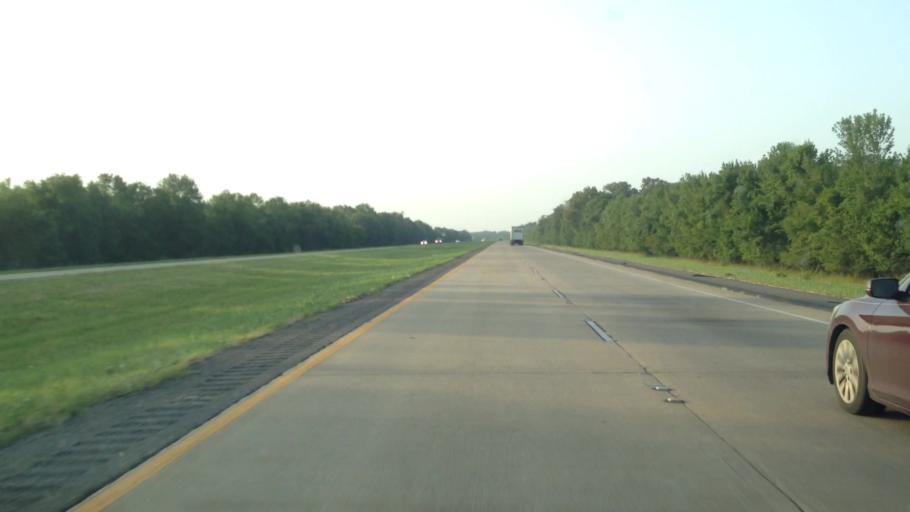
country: US
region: Louisiana
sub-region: Natchitoches Parish
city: Vienna Bend
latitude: 31.5903
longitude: -93.0323
